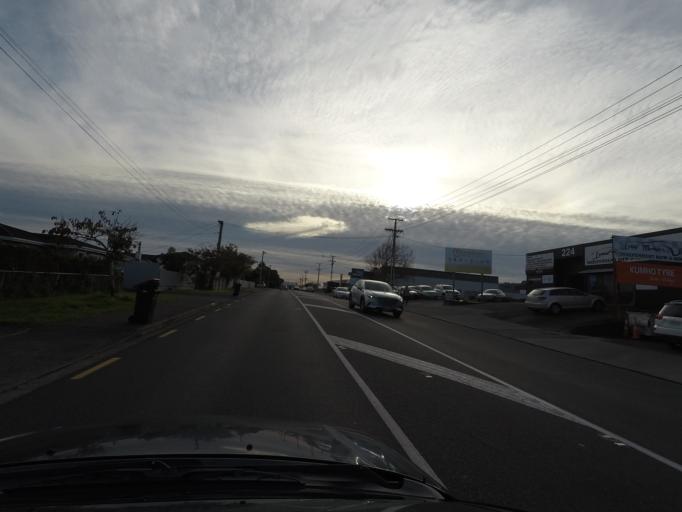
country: NZ
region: Auckland
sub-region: Auckland
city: Tamaki
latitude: -36.8941
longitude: 174.8361
